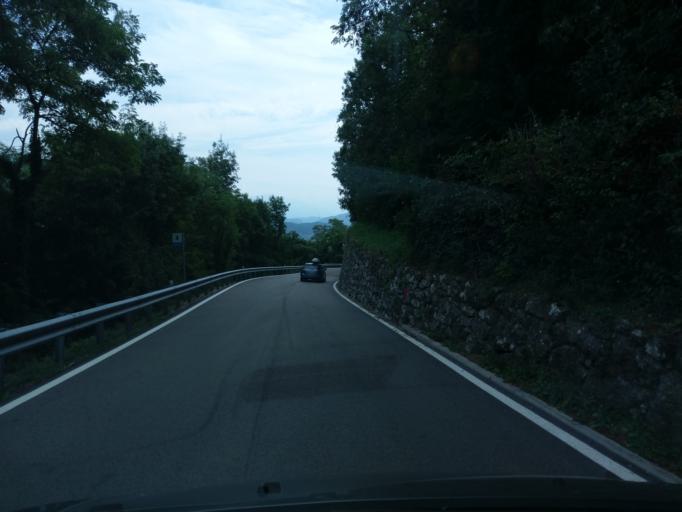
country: IT
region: Trentino-Alto Adige
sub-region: Provincia di Trento
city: Tenno
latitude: 45.9094
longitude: 10.8316
